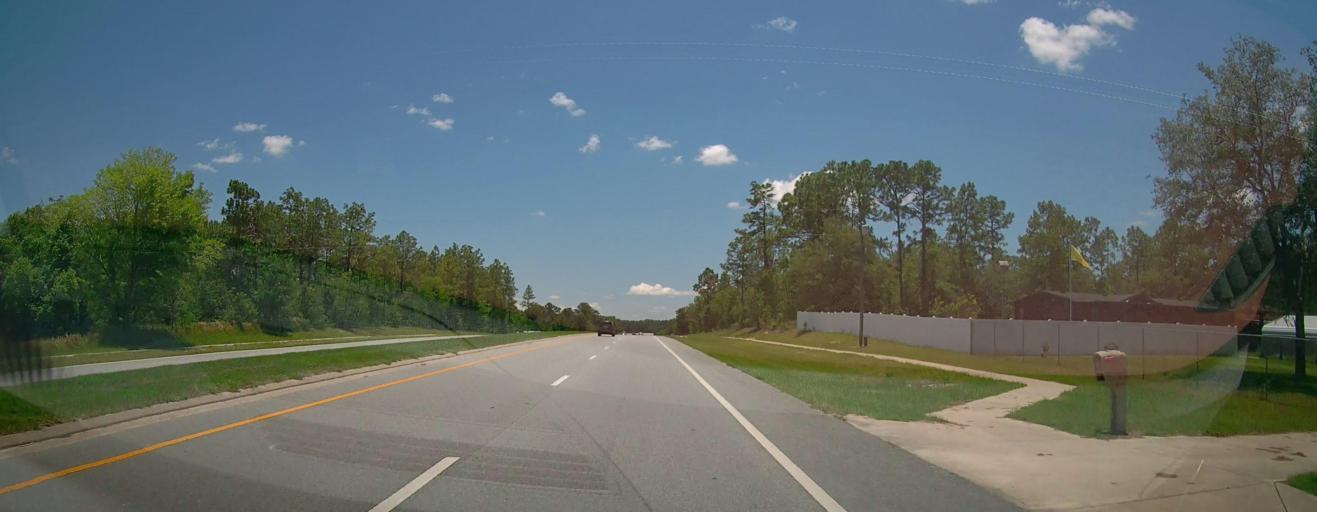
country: US
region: Florida
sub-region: Marion County
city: Belleview
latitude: 29.0450
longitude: -82.0176
